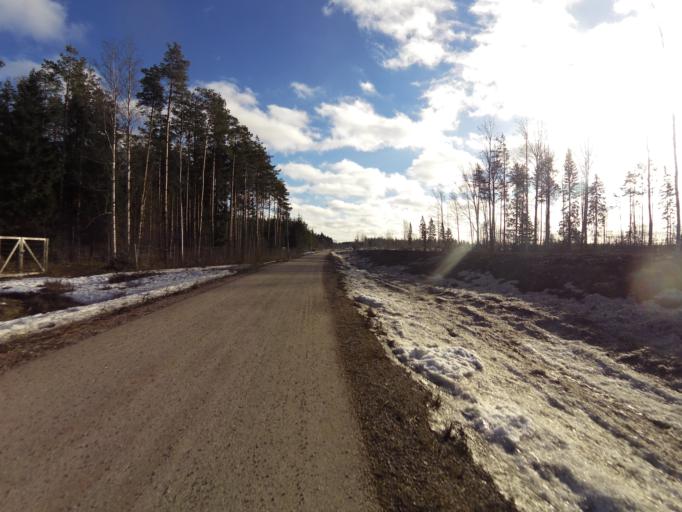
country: SE
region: Gaevleborg
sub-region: Gavle Kommun
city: Gavle
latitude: 60.6483
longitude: 17.2484
